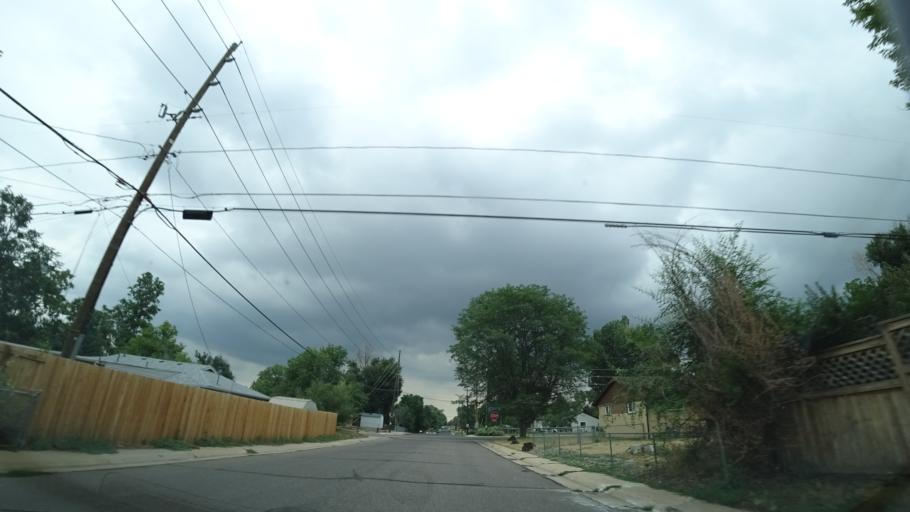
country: US
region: Colorado
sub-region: Jefferson County
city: Lakewood
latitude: 39.7073
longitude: -105.1291
